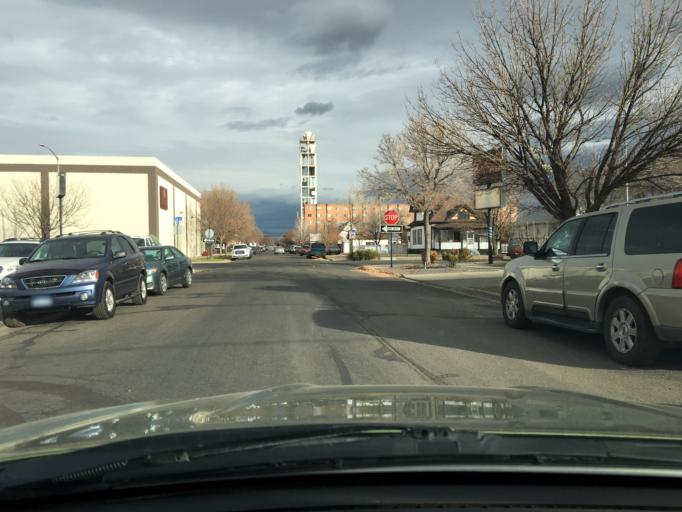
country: US
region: Colorado
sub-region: Mesa County
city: Grand Junction
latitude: 39.0649
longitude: -108.5594
